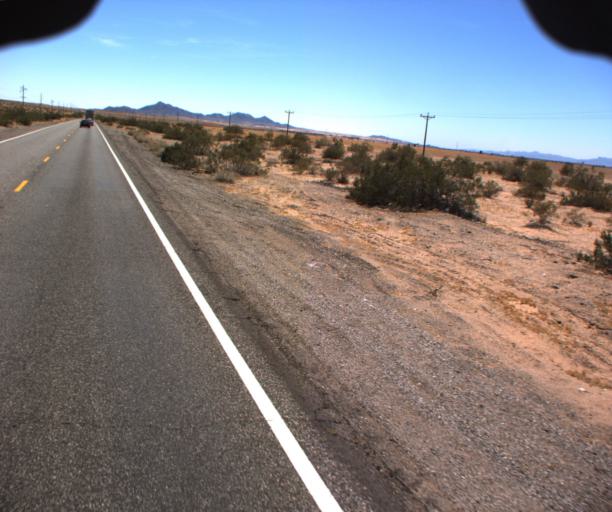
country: US
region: Arizona
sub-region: La Paz County
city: Parker
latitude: 34.1169
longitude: -114.2787
